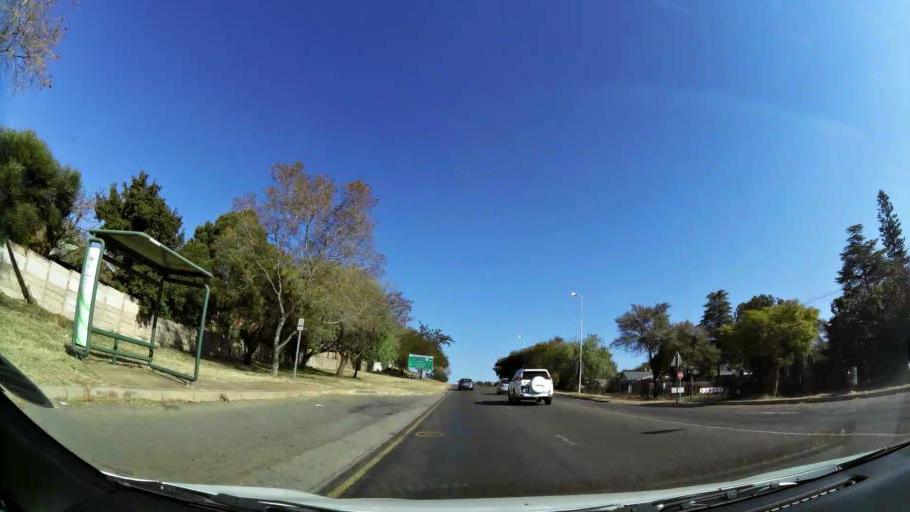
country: ZA
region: Gauteng
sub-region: City of Tshwane Metropolitan Municipality
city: Centurion
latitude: -25.8118
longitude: 28.2781
